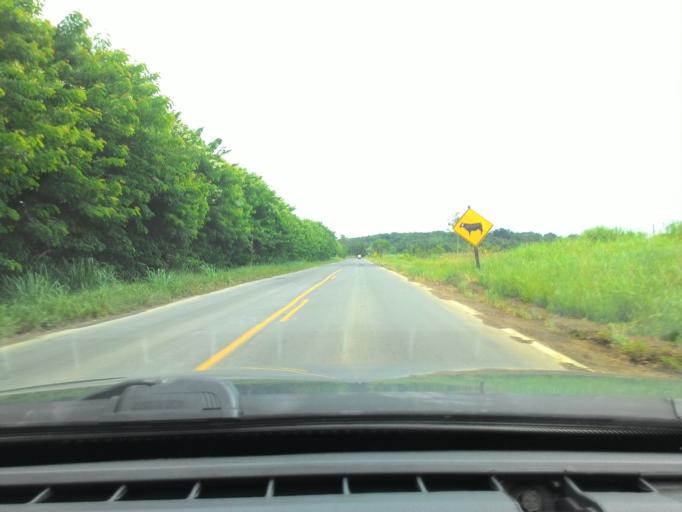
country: BR
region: Sao Paulo
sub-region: Pariquera-Acu
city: Pariquera Acu
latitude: -24.7364
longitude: -47.8166
